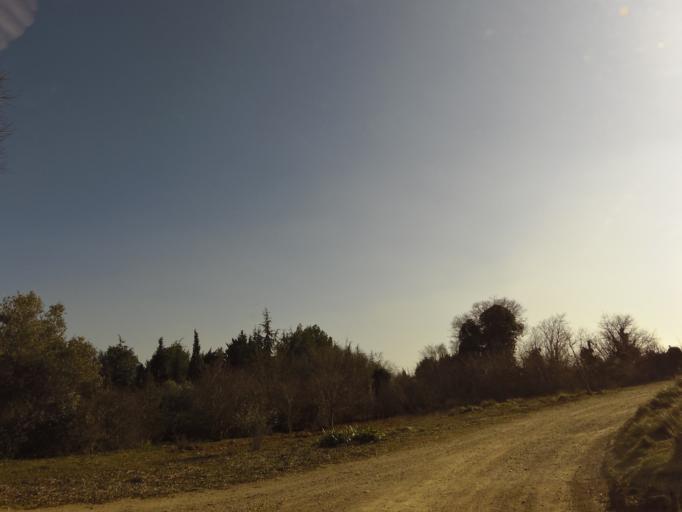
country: FR
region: Languedoc-Roussillon
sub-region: Departement du Gard
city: Codognan
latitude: 43.7312
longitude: 4.2134
